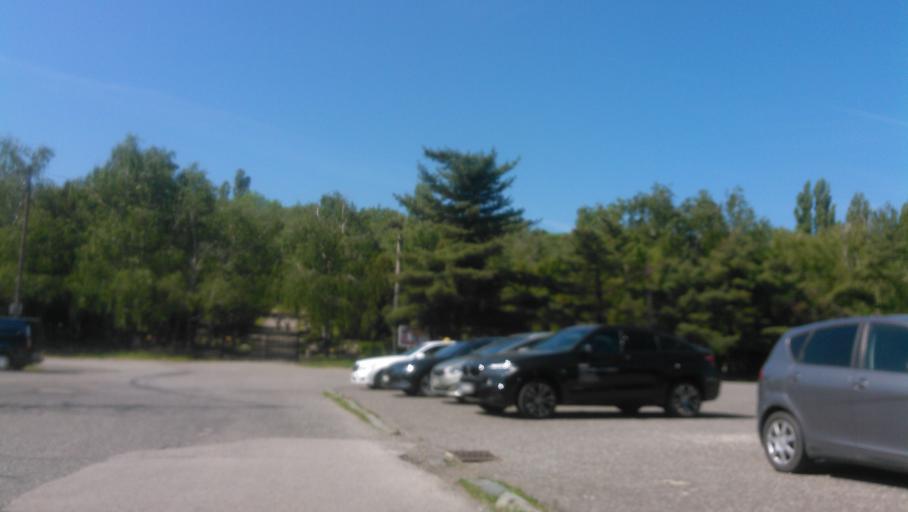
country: SK
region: Bratislavsky
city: Bratislava
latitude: 48.1564
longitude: 17.0714
